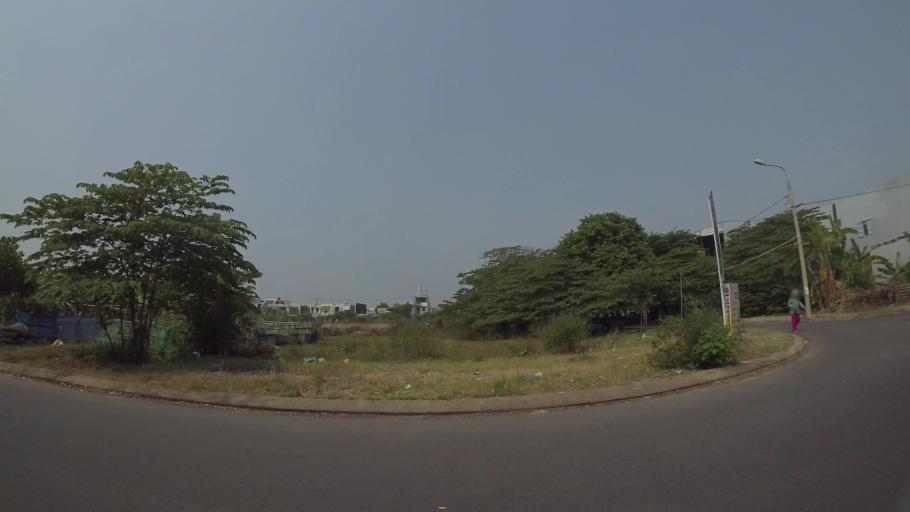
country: VN
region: Da Nang
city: Cam Le
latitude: 15.9813
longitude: 108.2141
